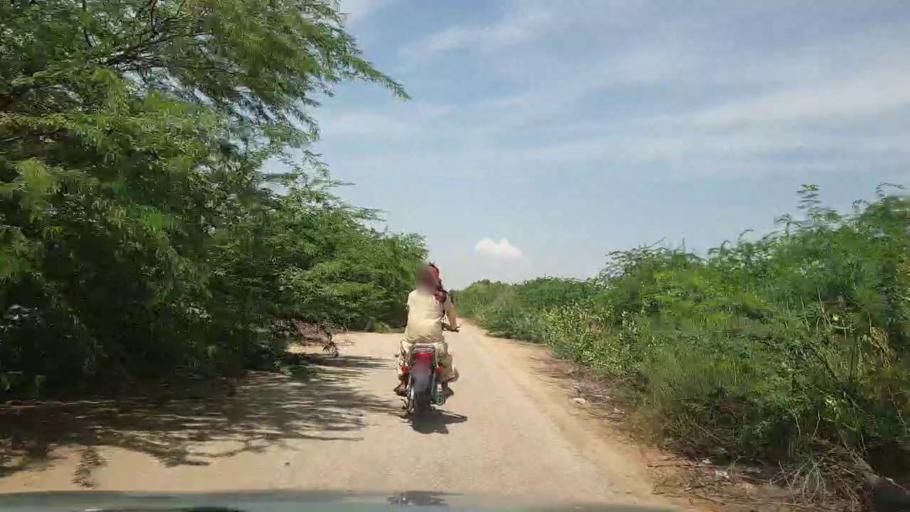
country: PK
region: Sindh
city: Bozdar
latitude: 27.0895
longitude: 68.9999
